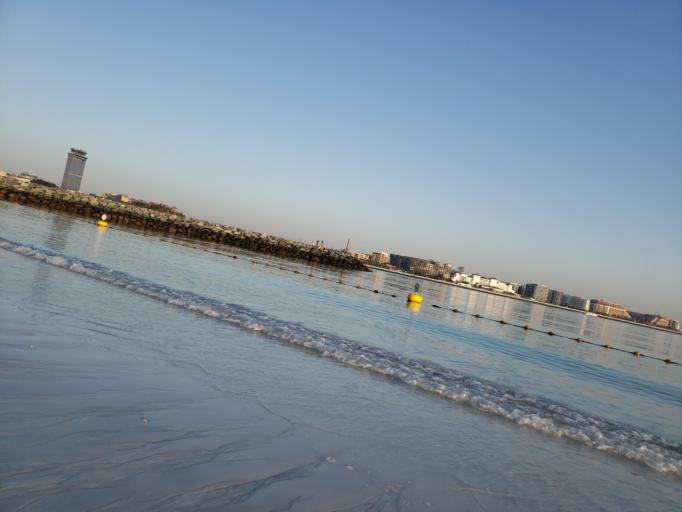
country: AE
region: Dubai
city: Dubai
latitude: 25.1163
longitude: 55.1653
